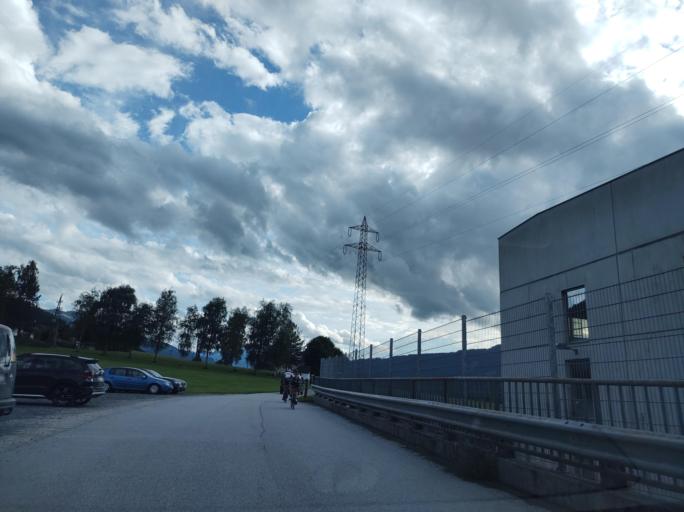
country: AT
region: Tyrol
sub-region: Politischer Bezirk Kitzbuhel
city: Oberndorf in Tirol
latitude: 47.5040
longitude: 12.4011
